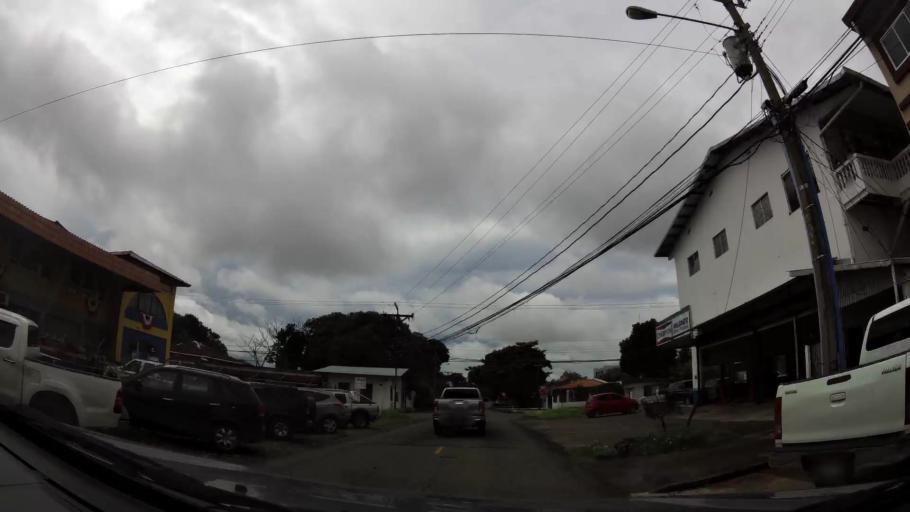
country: PA
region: Chiriqui
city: David
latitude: 8.4278
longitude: -82.4314
